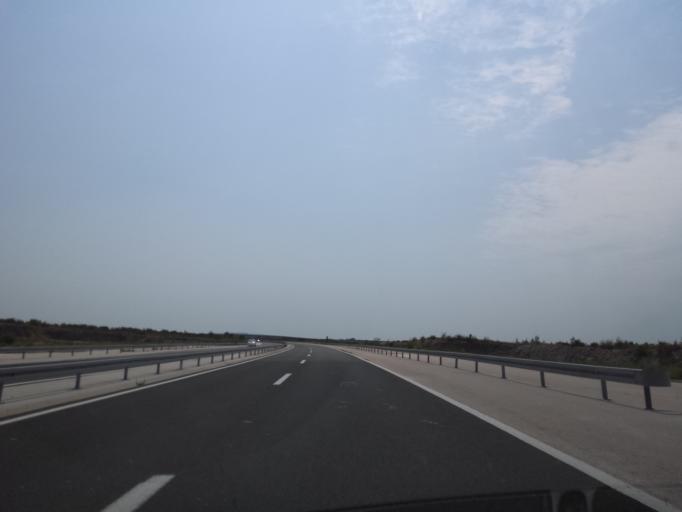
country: HR
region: Zadarska
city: Policnik
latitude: 44.1389
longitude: 15.4201
